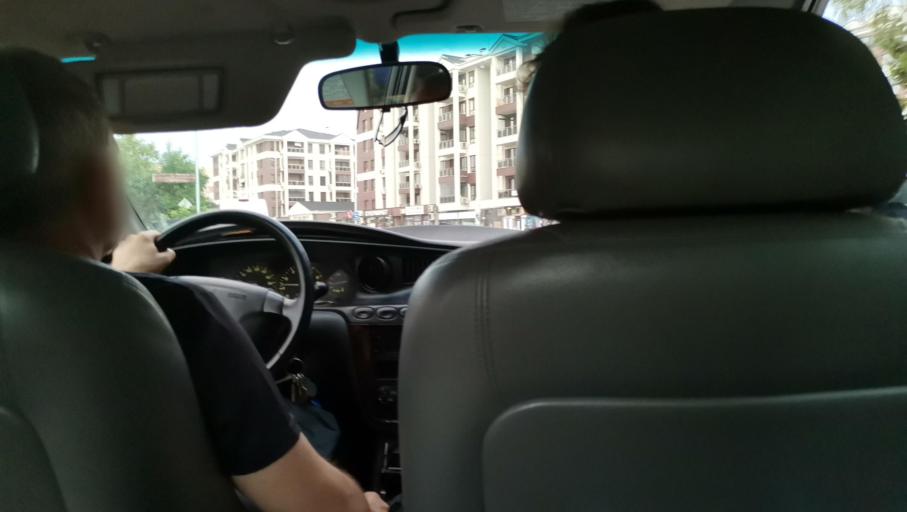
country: BG
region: Plovdiv
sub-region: Obshtina Plovdiv
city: Plovdiv
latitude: 42.1399
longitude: 24.7874
